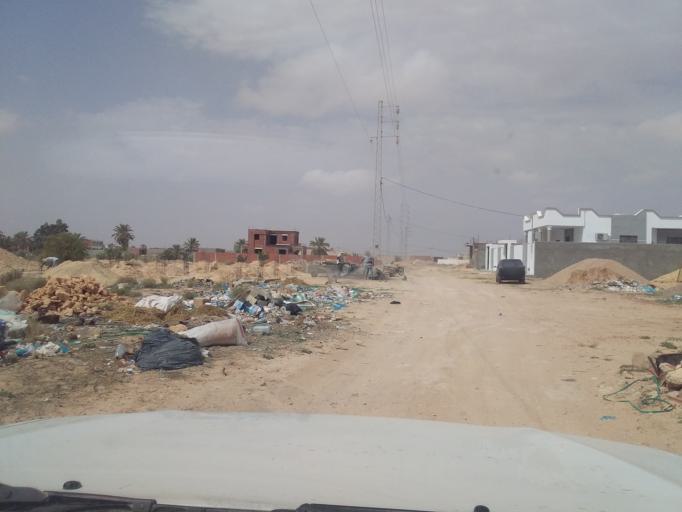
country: TN
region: Qabis
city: Matmata
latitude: 33.6203
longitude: 10.2717
